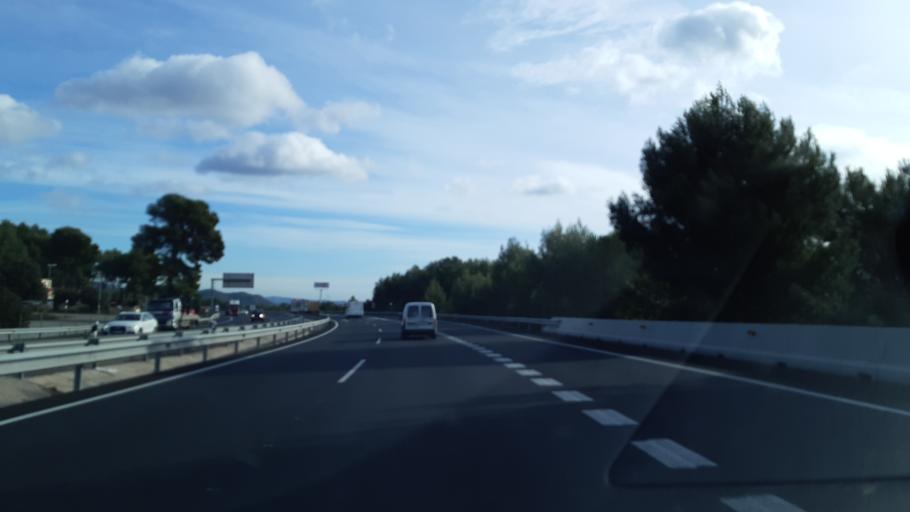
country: ES
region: Catalonia
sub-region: Provincia de Barcelona
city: Collbato
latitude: 41.5692
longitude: 1.7975
